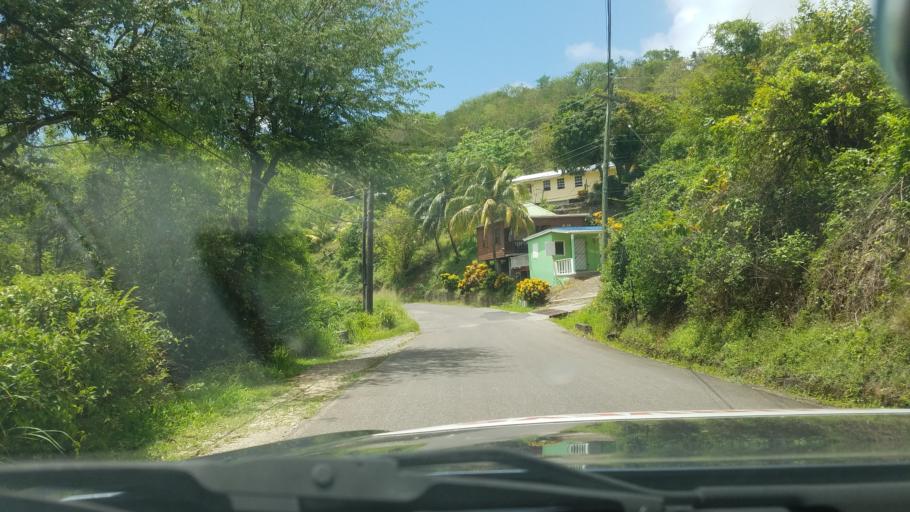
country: LC
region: Gros-Islet
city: Gros Islet
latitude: 14.0558
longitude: -60.9362
